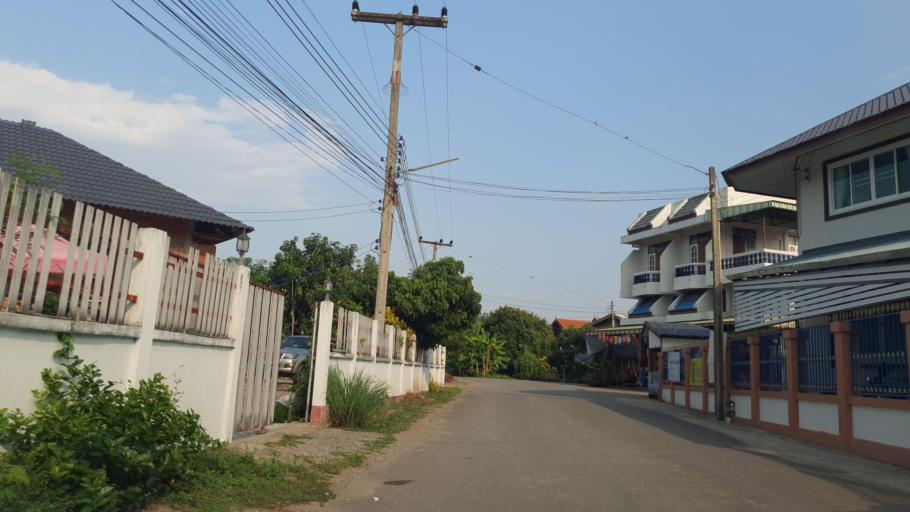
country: TH
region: Chiang Mai
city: Mae Wang
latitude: 18.6733
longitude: 98.8124
